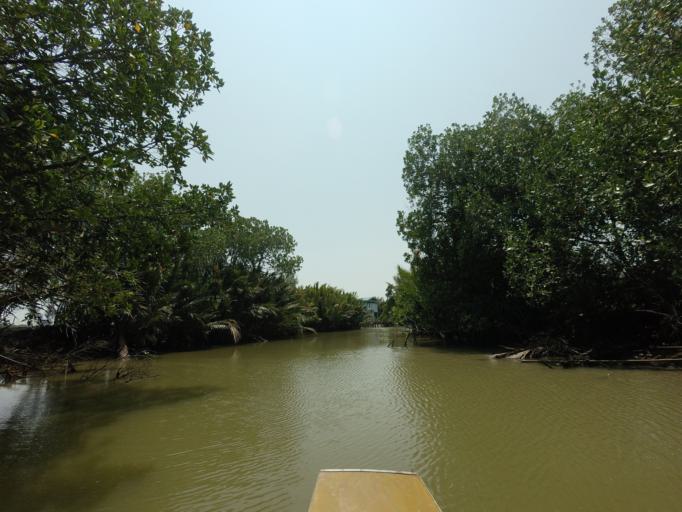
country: TH
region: Bangkok
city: Thung Khru
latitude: 13.5451
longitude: 100.4952
